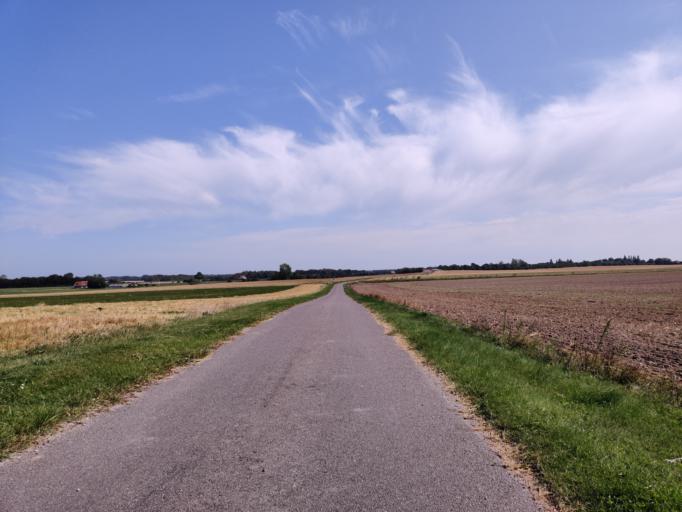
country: DK
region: Zealand
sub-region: Guldborgsund Kommune
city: Nykobing Falster
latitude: 54.6858
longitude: 11.8888
